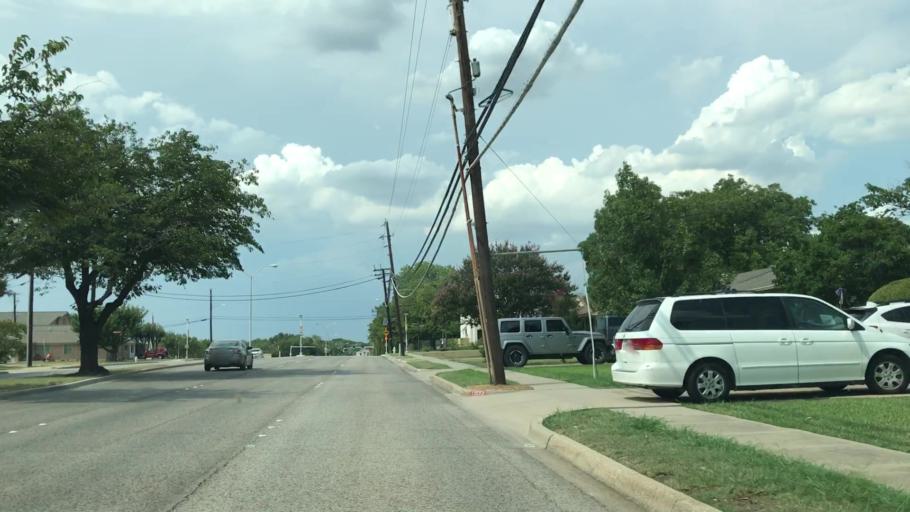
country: US
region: Texas
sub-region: Dallas County
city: Farmers Branch
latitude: 32.9304
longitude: -96.8731
